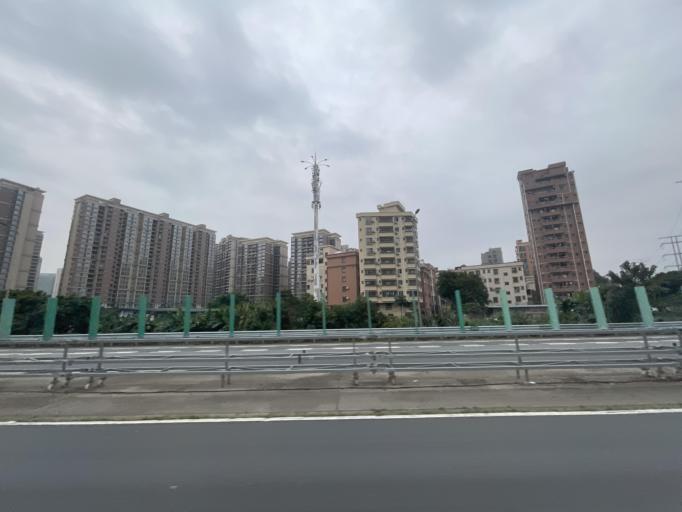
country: CN
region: Guangdong
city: Humen
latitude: 22.8090
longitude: 113.6880
